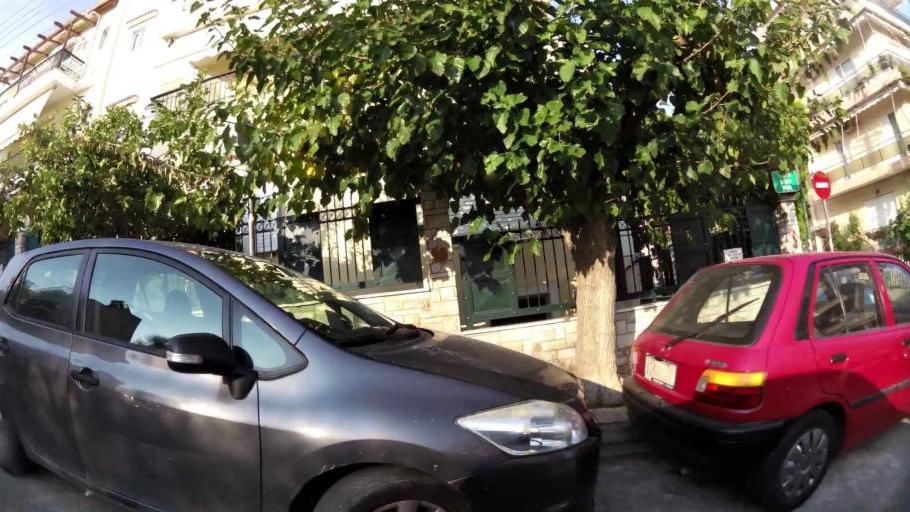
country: GR
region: Attica
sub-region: Nomarchia Athinas
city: Petroupolis
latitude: 38.0457
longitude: 23.6827
